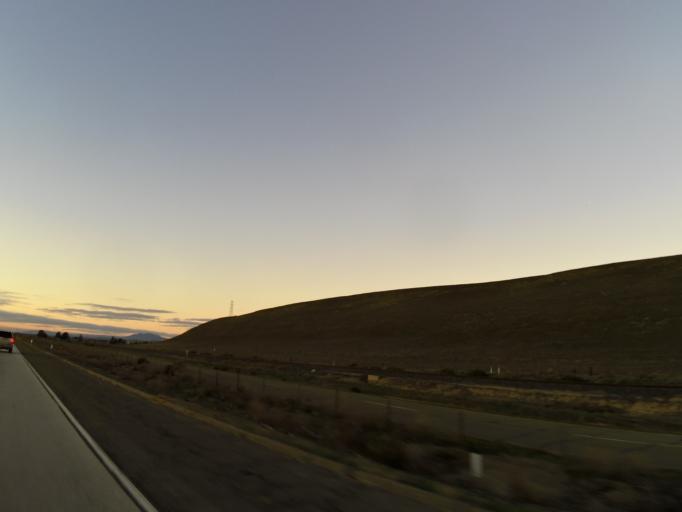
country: US
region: California
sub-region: Monterey County
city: King City
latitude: 36.1590
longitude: -121.0490
